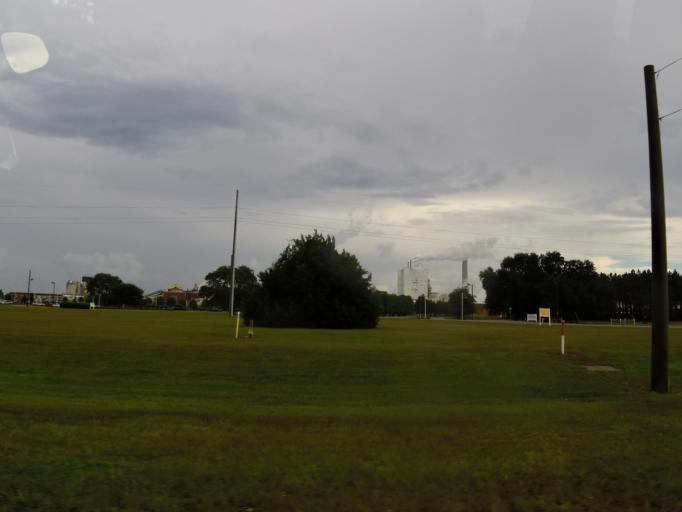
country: US
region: Georgia
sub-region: Wayne County
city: Jesup
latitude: 31.6615
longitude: -81.8478
